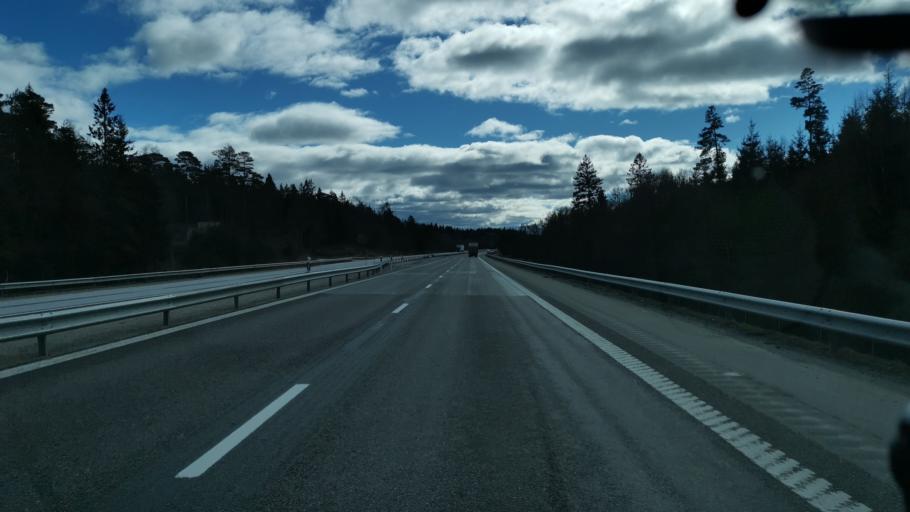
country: SE
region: Vaestra Goetaland
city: Svanesund
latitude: 58.1380
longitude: 11.8852
